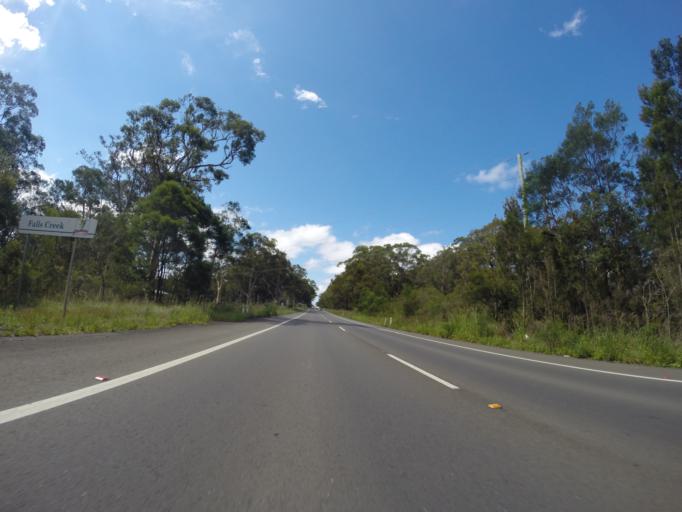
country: AU
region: New South Wales
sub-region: Shoalhaven Shire
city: Falls Creek
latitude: -35.0059
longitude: 150.5824
